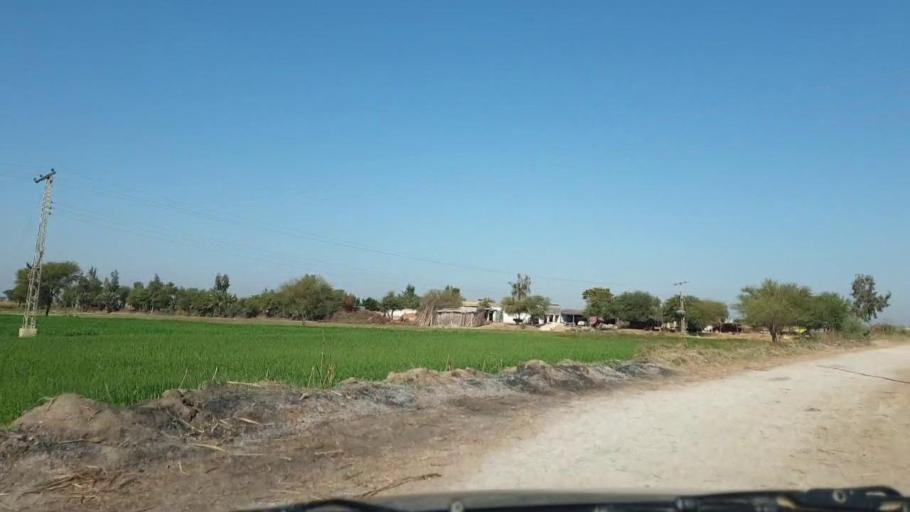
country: PK
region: Sindh
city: Sinjhoro
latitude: 26.1099
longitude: 68.8400
